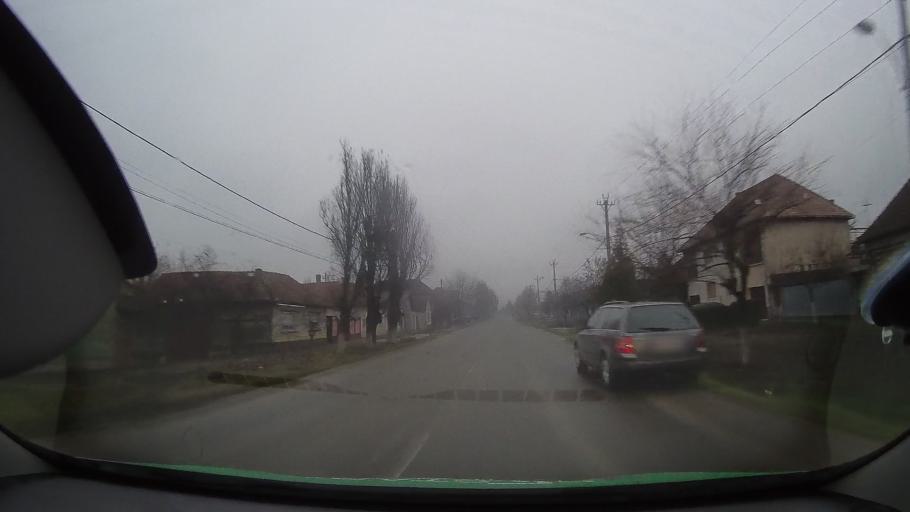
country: RO
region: Bihor
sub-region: Municipiul Salonta
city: Salonta
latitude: 46.8010
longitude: 21.6479
